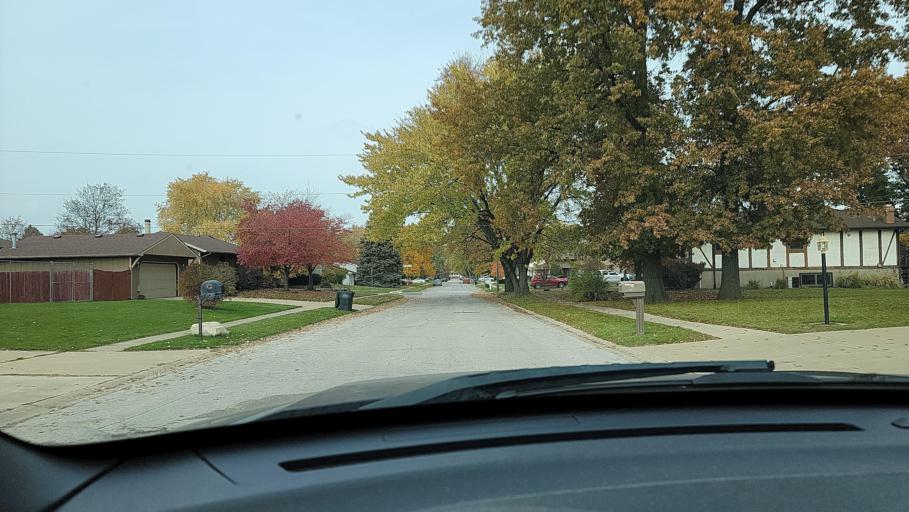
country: US
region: Indiana
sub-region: Porter County
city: Portage
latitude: 41.5893
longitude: -87.1558
